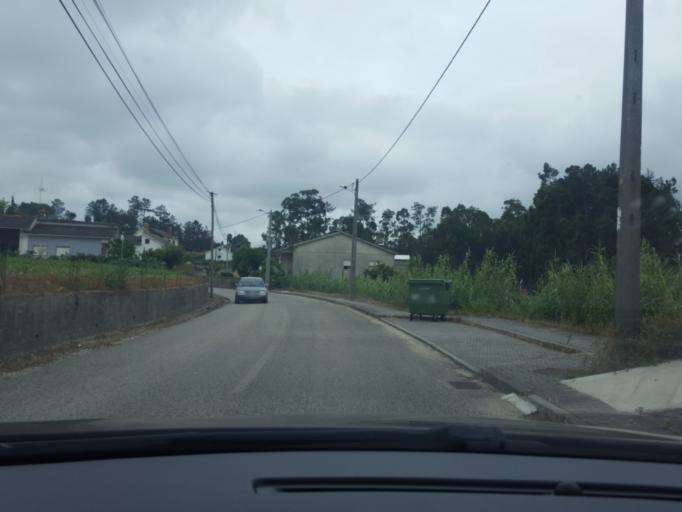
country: PT
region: Leiria
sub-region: Leiria
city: Caranguejeira
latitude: 39.7926
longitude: -8.7509
